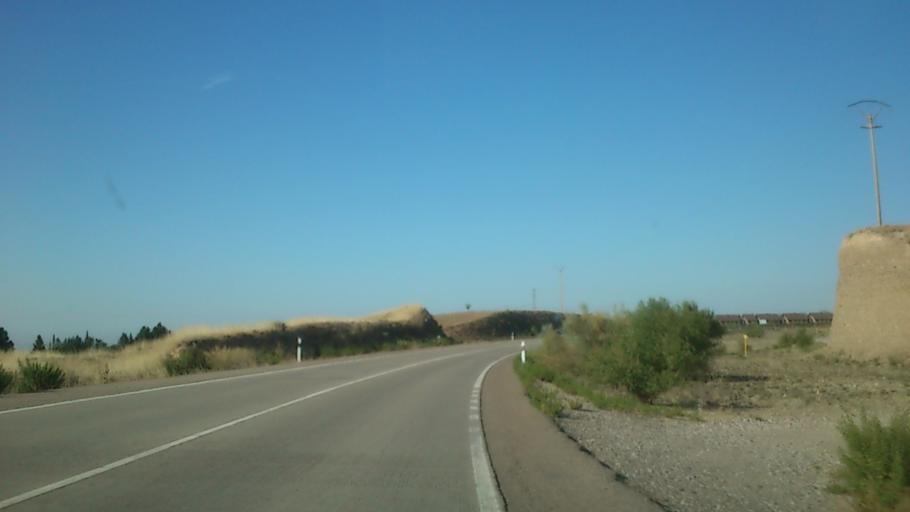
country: ES
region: Aragon
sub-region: Provincia de Zaragoza
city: Villanueva de Gallego
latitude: 41.7824
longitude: -0.8164
